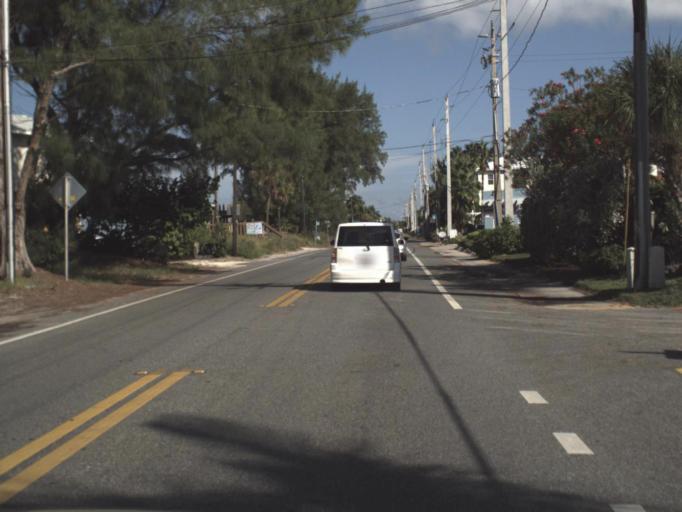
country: US
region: Florida
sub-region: Manatee County
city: Bradenton Beach
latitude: 27.4721
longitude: -82.7009
